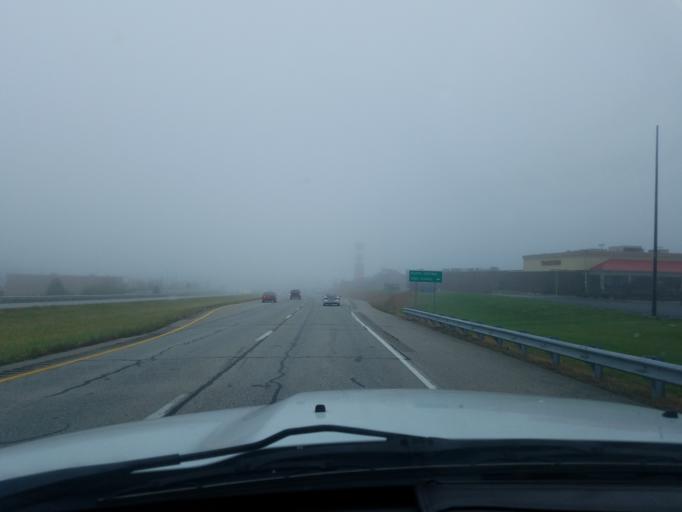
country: US
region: Indiana
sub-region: Floyd County
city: Galena
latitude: 38.3174
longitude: -85.8983
